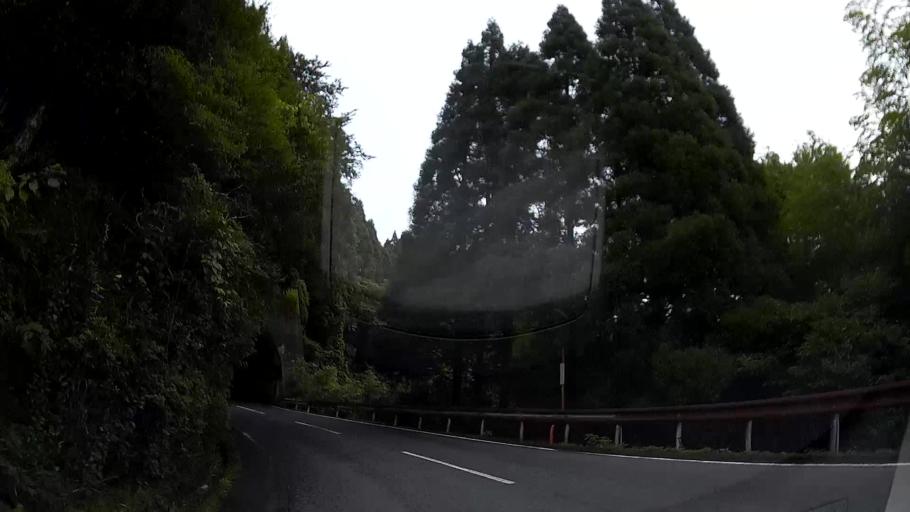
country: JP
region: Kumamoto
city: Kikuchi
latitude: 33.0941
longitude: 130.9564
